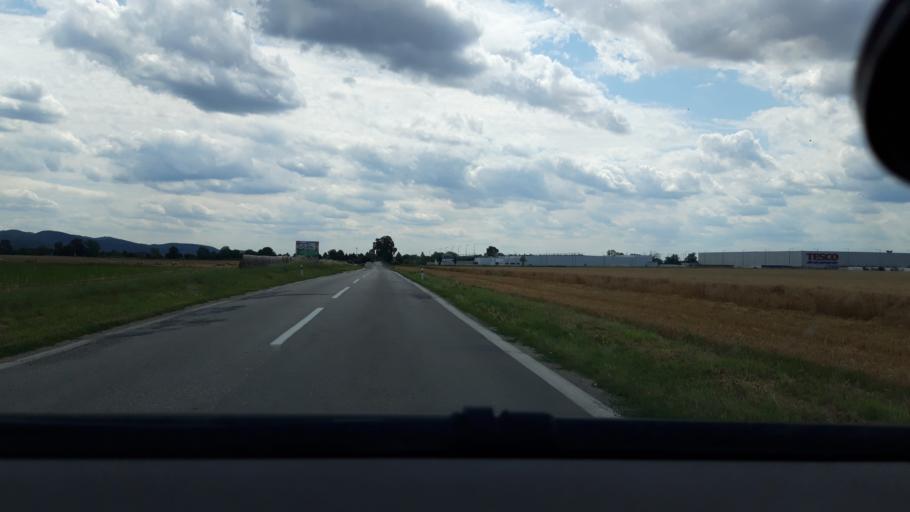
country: SK
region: Trenciansky
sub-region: Okres Nove Mesto nad Vahom
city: Nove Mesto nad Vahom
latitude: 48.7709
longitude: 17.8906
